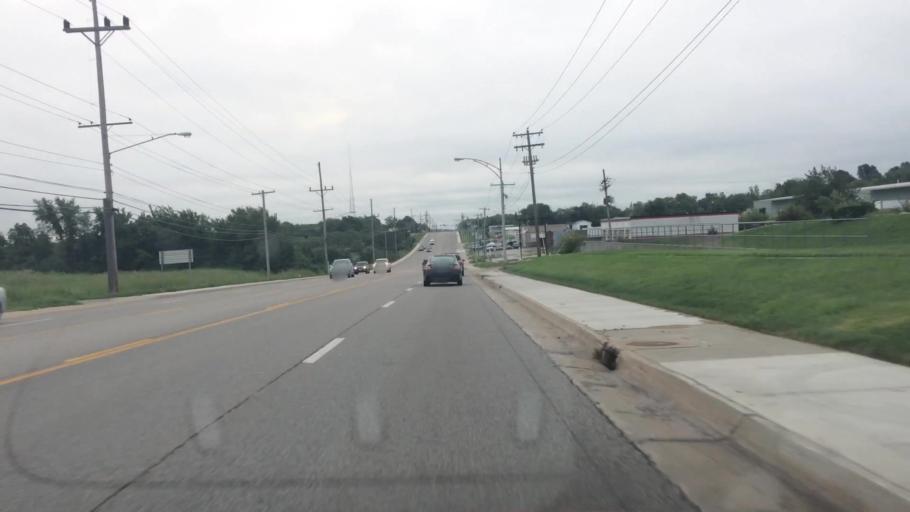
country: US
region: Missouri
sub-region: Greene County
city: Springfield
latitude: 37.2394
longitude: -93.2416
